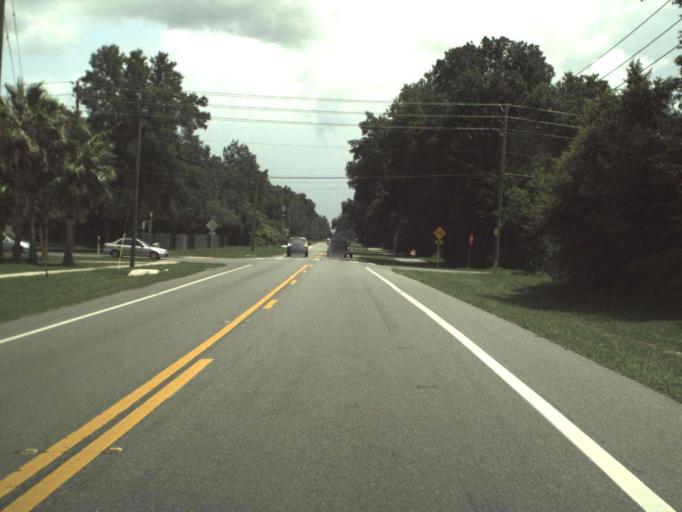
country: US
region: Florida
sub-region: Sumter County
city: Bushnell
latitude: 28.6679
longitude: -82.1043
